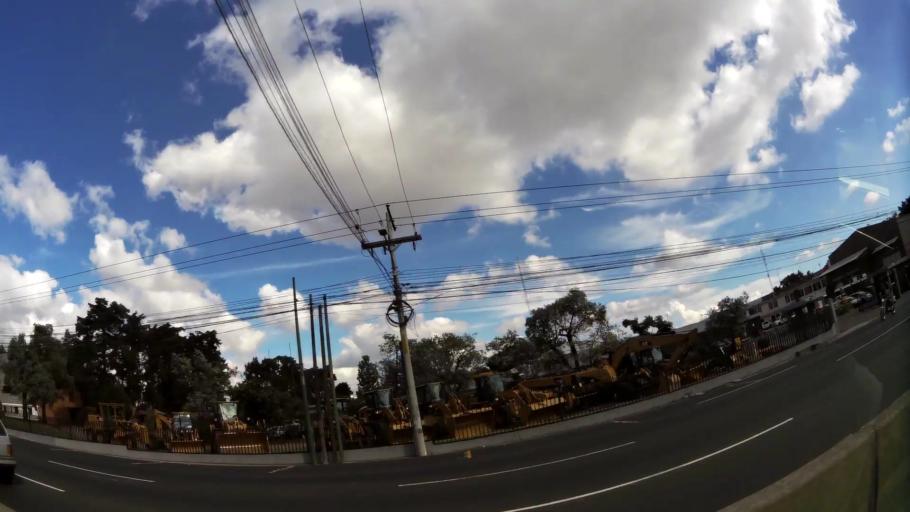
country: GT
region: Guatemala
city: Villa Nueva
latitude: 14.5681
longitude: -90.5740
